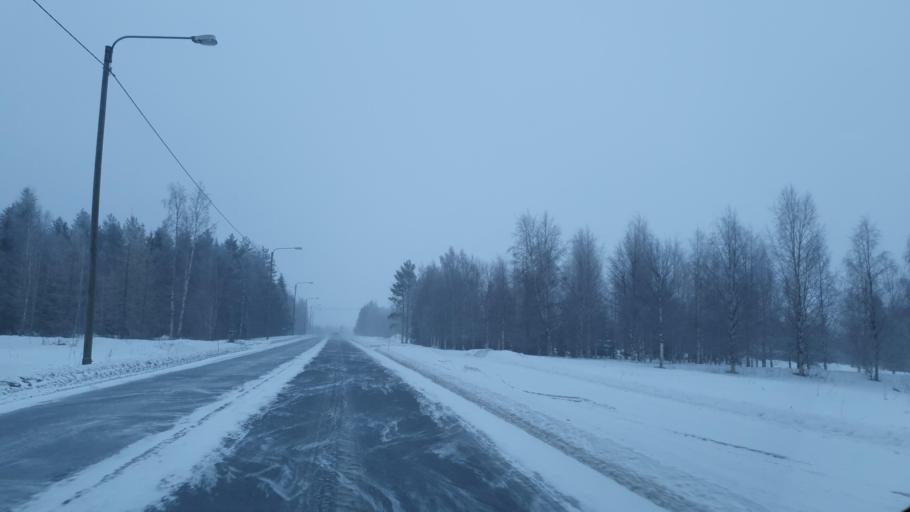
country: FI
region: Lapland
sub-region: Kemi-Tornio
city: Tornio
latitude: 65.9448
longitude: 24.0801
